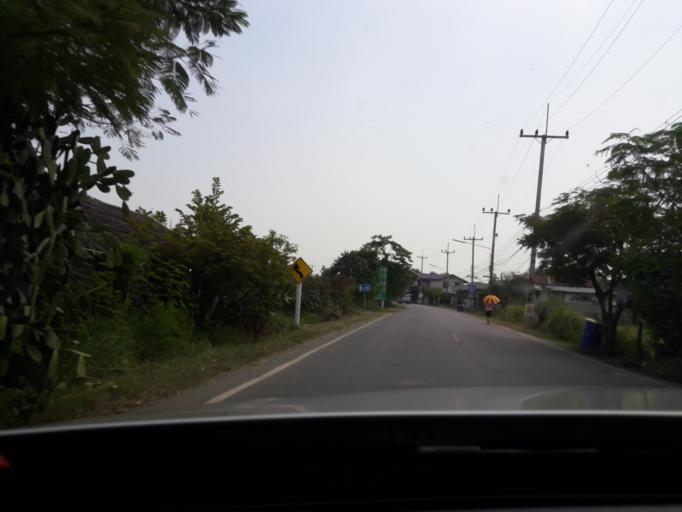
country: TH
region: Samut Songkhram
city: Amphawa
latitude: 13.3380
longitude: 99.9600
